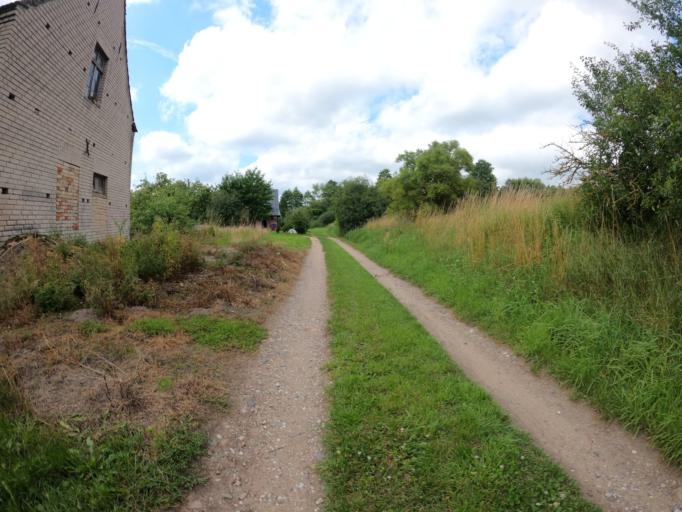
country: PL
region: West Pomeranian Voivodeship
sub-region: Powiat szczecinecki
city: Grzmiaca
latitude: 53.8015
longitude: 16.4715
